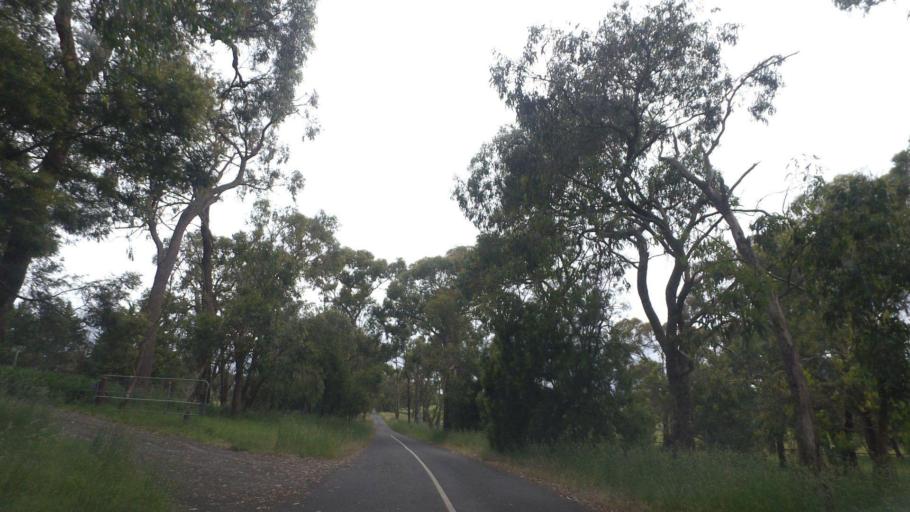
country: AU
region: Victoria
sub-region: Yarra Ranges
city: Mount Evelyn
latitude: -37.7392
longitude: 145.4163
